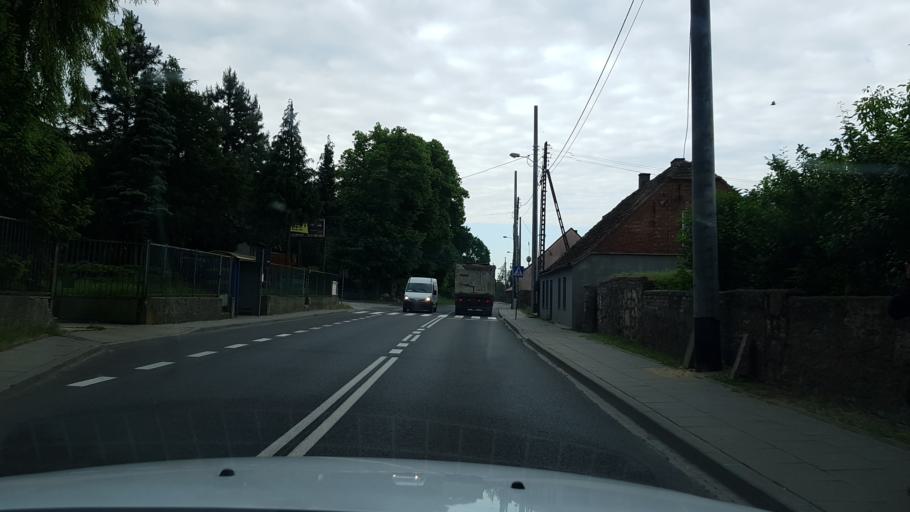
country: PL
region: West Pomeranian Voivodeship
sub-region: Powiat gryfinski
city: Gryfino
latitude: 53.3151
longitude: 14.5346
